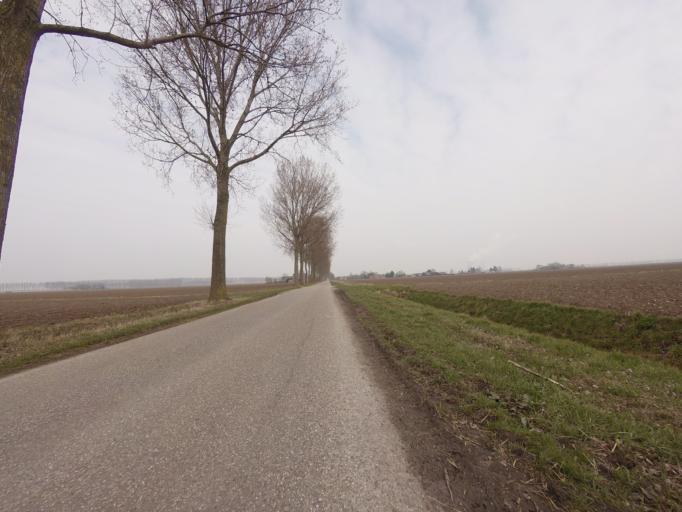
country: BE
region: Flanders
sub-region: Provincie Oost-Vlaanderen
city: Beveren
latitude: 51.3210
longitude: 4.1963
